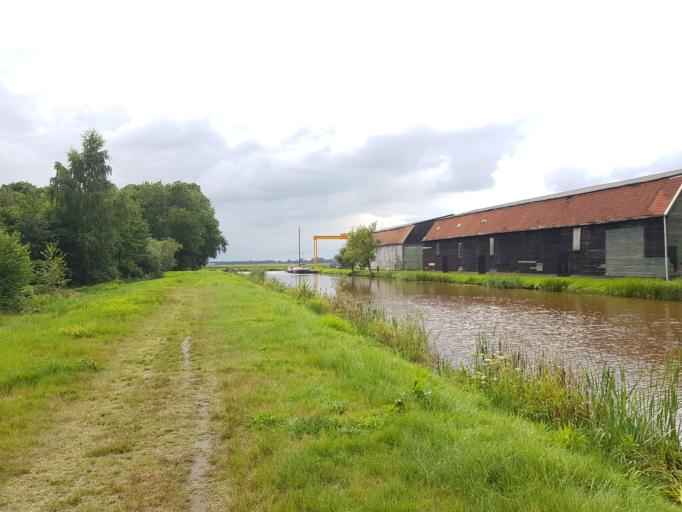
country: NL
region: Groningen
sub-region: Gemeente Hoogezand-Sappemeer
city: Hoogezand
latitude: 53.2159
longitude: 6.7436
